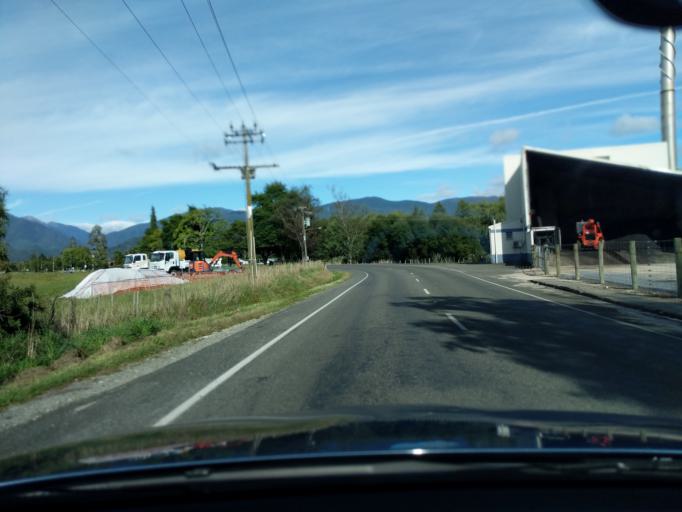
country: NZ
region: Tasman
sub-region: Tasman District
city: Takaka
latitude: -40.8554
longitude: 172.8152
